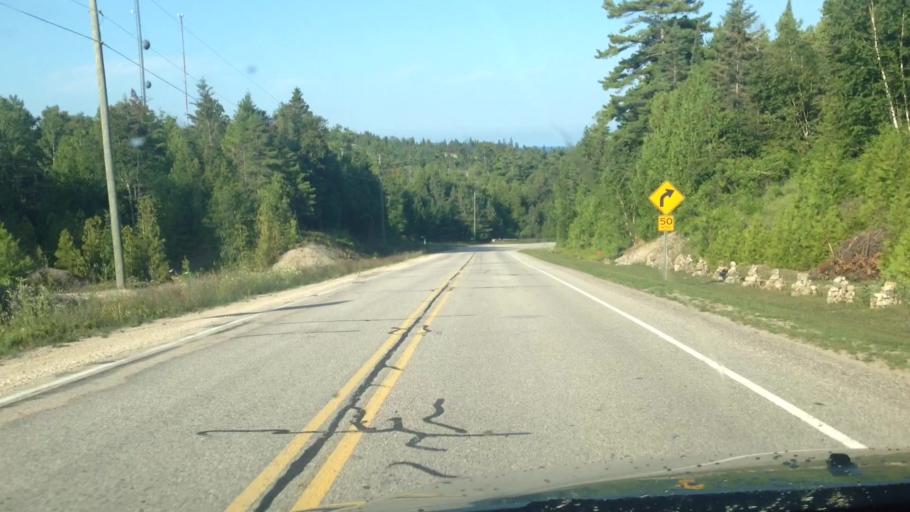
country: US
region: Michigan
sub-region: Mackinac County
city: Saint Ignace
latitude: 45.8931
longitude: -84.8251
